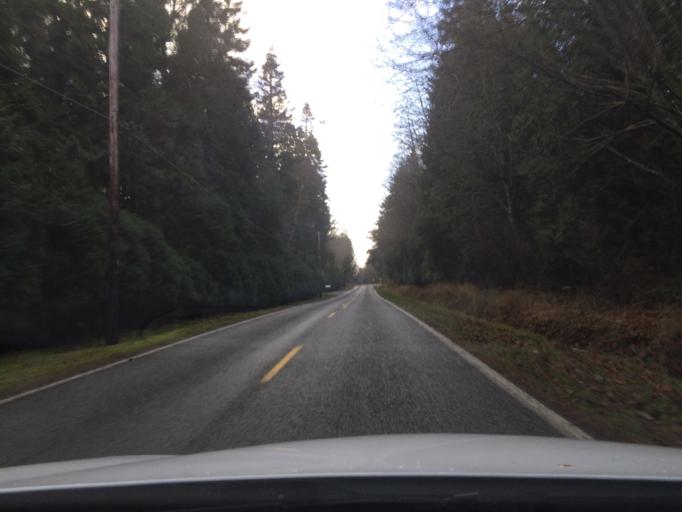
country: US
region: Washington
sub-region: Whatcom County
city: Birch Bay
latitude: 48.9406
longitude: -122.8139
